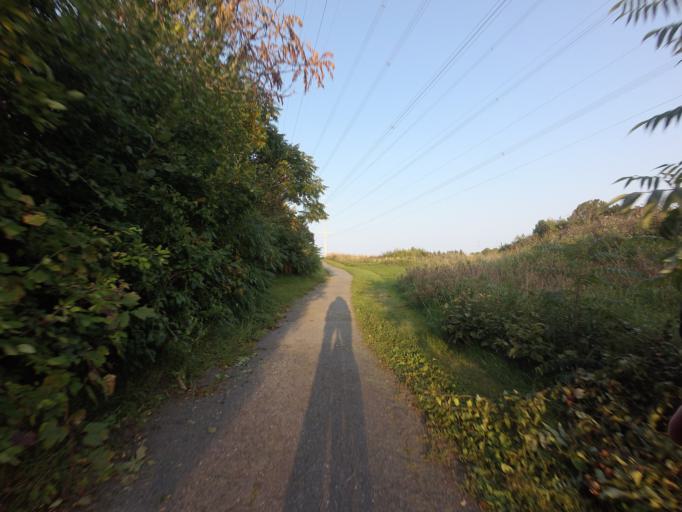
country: CA
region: Ontario
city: Bells Corners
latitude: 45.2857
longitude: -75.8643
